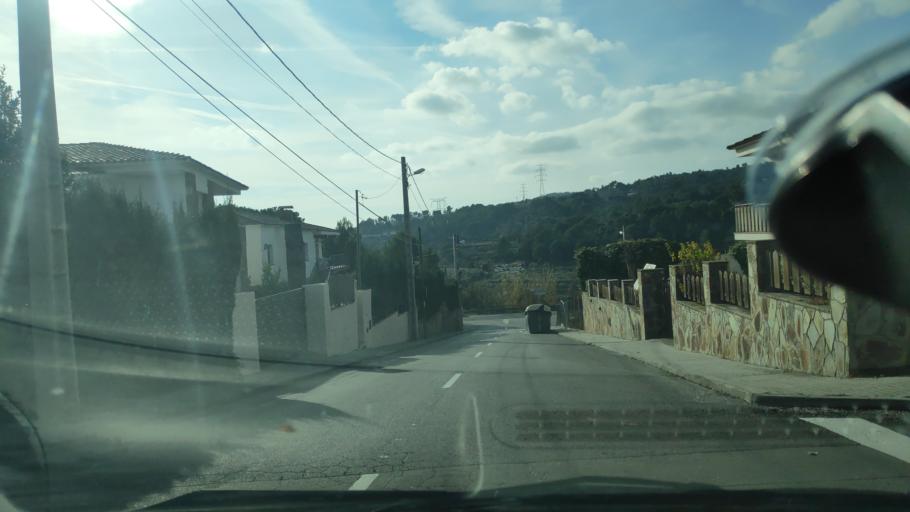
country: ES
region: Catalonia
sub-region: Provincia de Barcelona
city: Castellar del Valles
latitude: 41.6185
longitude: 2.0817
